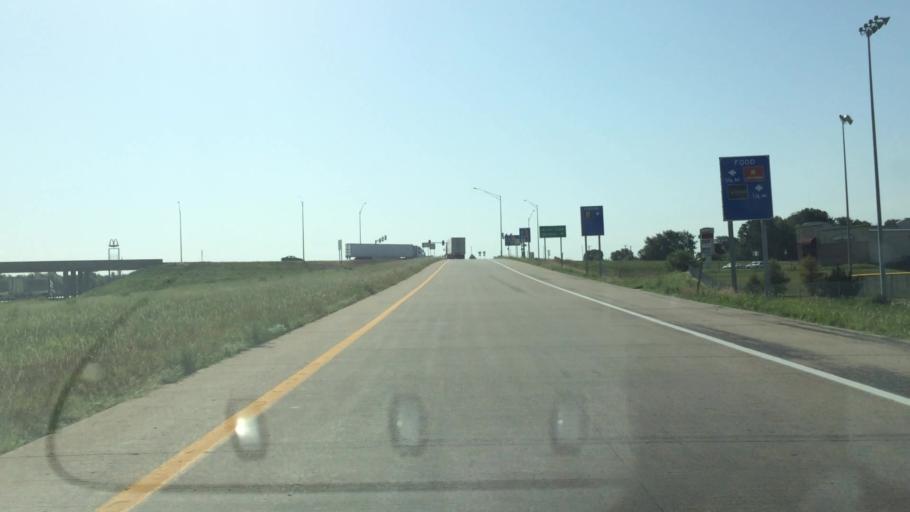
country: US
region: Missouri
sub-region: Greene County
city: Strafford
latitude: 37.2724
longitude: -93.1156
